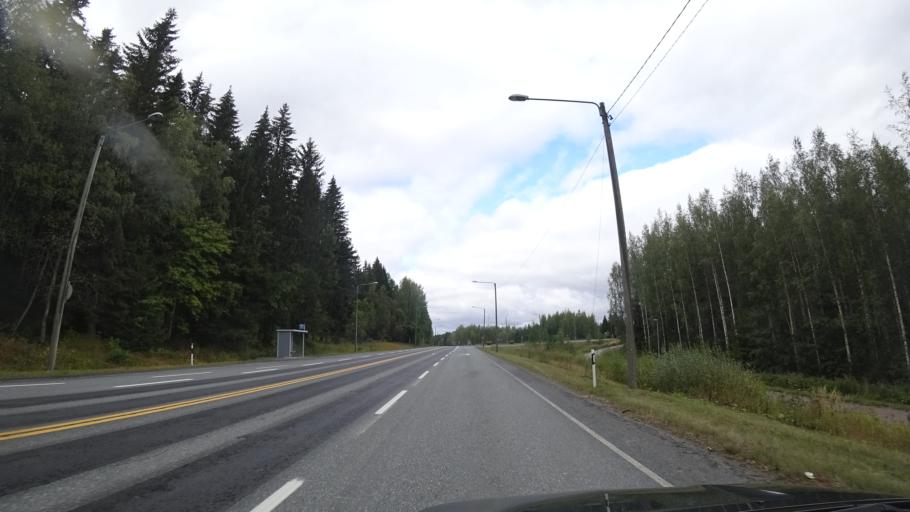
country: FI
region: Haeme
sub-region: Haemeenlinna
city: Lammi
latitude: 61.0527
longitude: 25.0073
